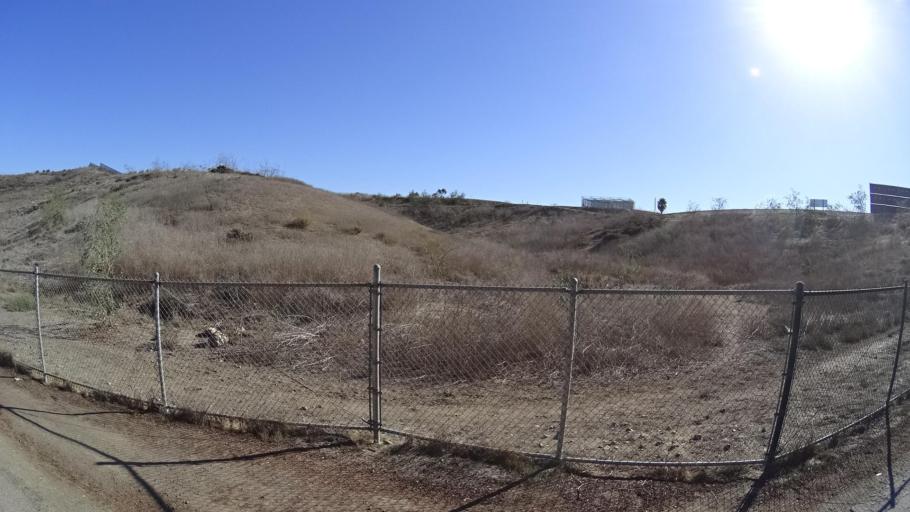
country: US
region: California
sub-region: San Diego County
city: Bonita
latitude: 32.6794
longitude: -117.0088
